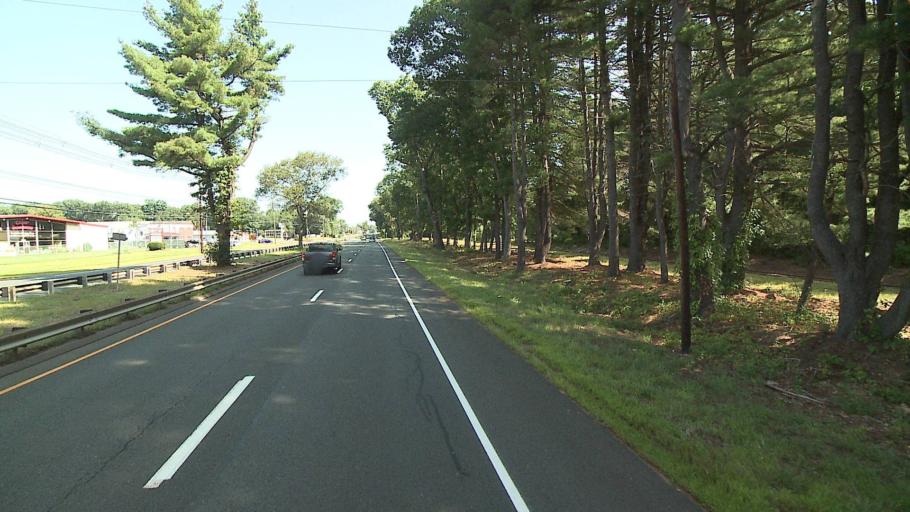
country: US
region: Connecticut
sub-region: Hartford County
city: South Windsor
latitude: 41.8356
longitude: -72.6032
